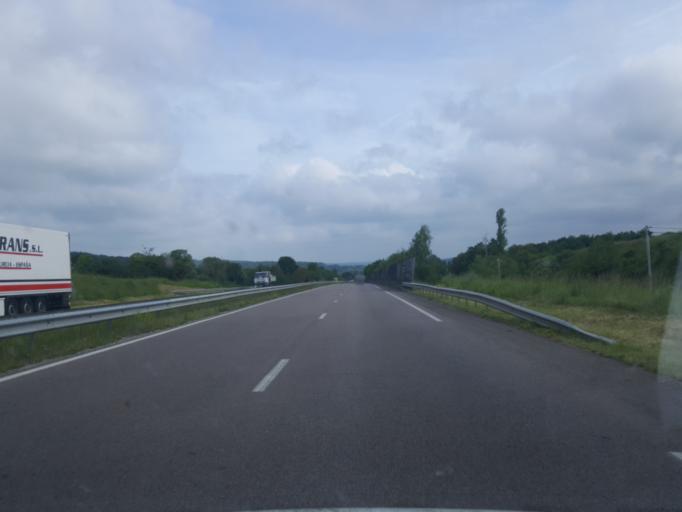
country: FR
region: Haute-Normandie
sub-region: Departement de l'Eure
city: Heudreville-sur-Eure
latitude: 49.1337
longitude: 1.1828
